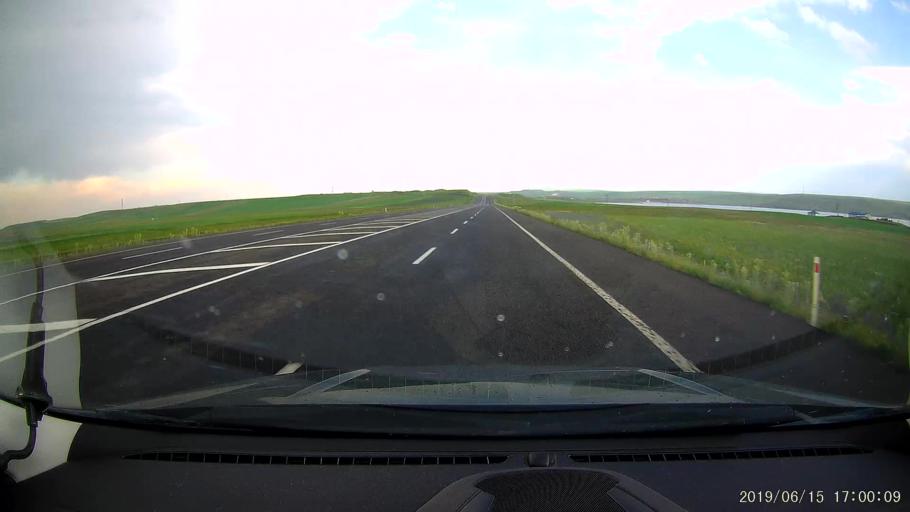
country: TR
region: Kars
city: Susuz
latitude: 40.7429
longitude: 43.1583
